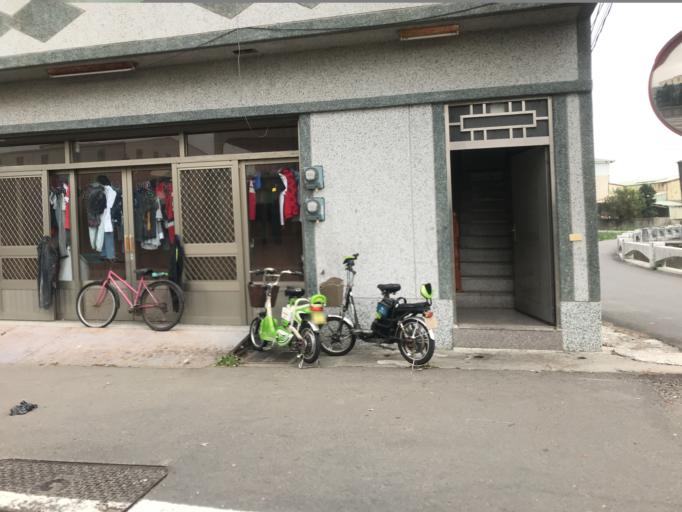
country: TW
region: Taiwan
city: Fengyuan
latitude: 24.3547
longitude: 120.6105
